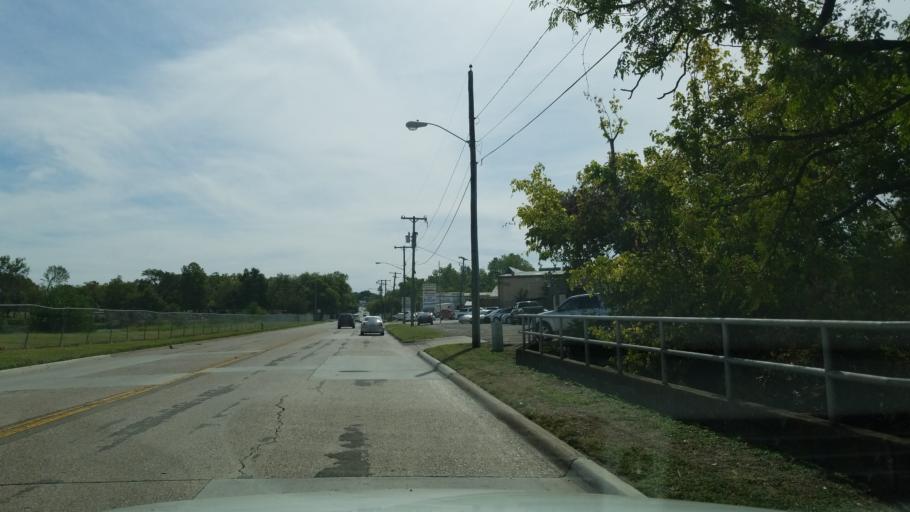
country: US
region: Texas
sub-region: Dallas County
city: Highland Park
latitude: 32.7915
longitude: -96.7259
